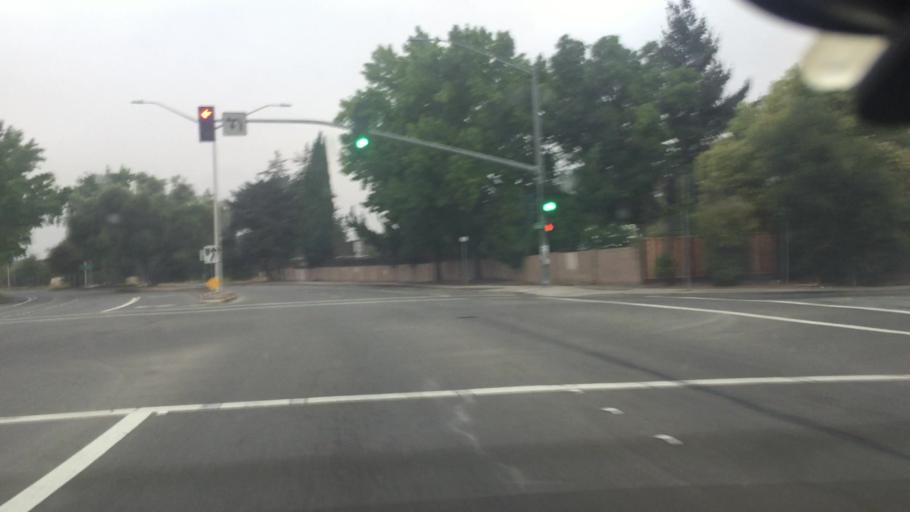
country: US
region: California
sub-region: Alameda County
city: Fremont
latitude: 37.5423
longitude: -121.9498
